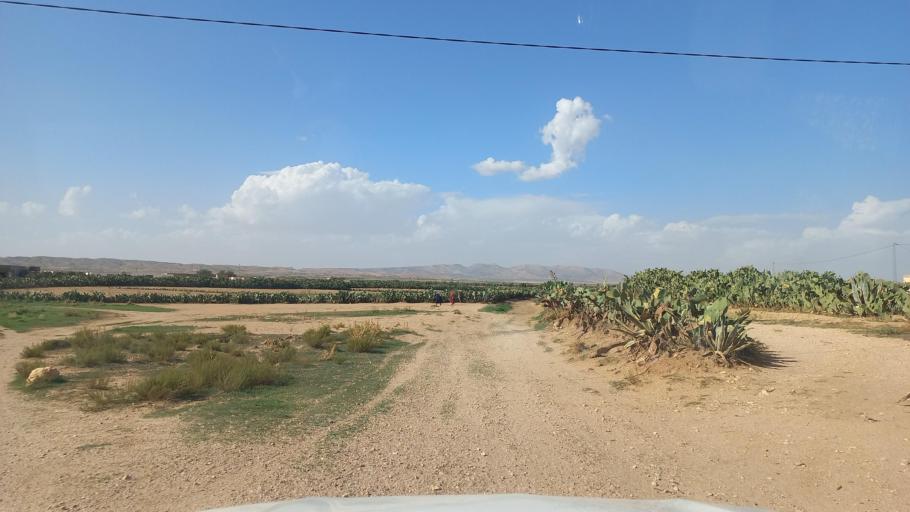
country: TN
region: Al Qasrayn
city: Sbiba
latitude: 35.3170
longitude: 9.0293
